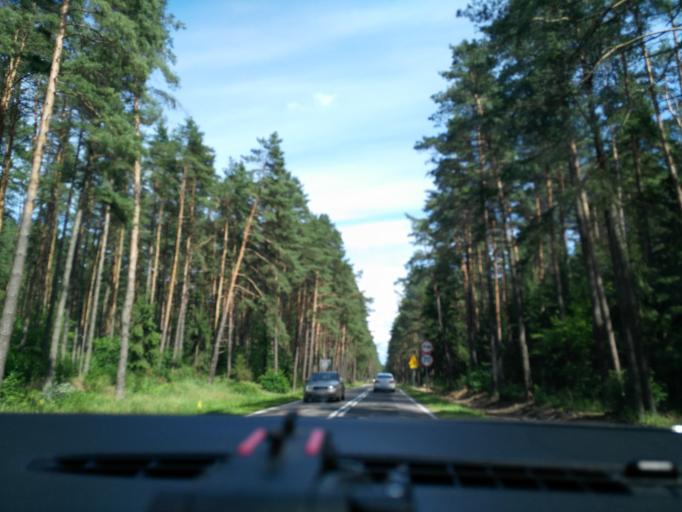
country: PL
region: Podlasie
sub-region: Powiat augustowski
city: Augustow
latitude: 53.8539
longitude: 23.0558
